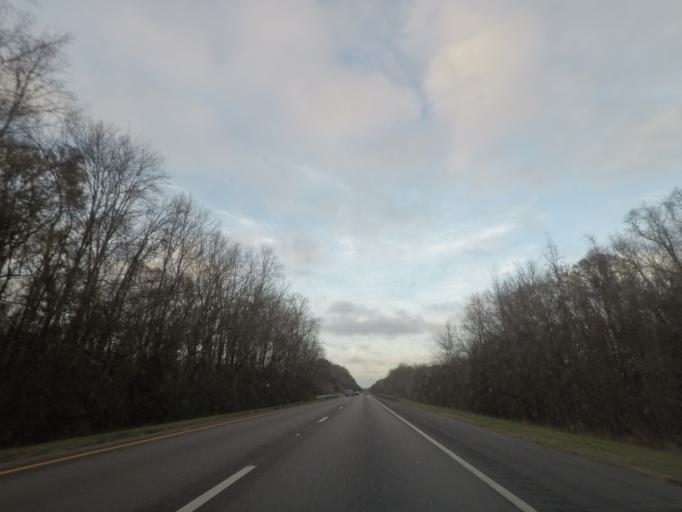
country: US
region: South Carolina
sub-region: Orangeburg County
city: Holly Hill
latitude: 33.3371
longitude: -80.5365
